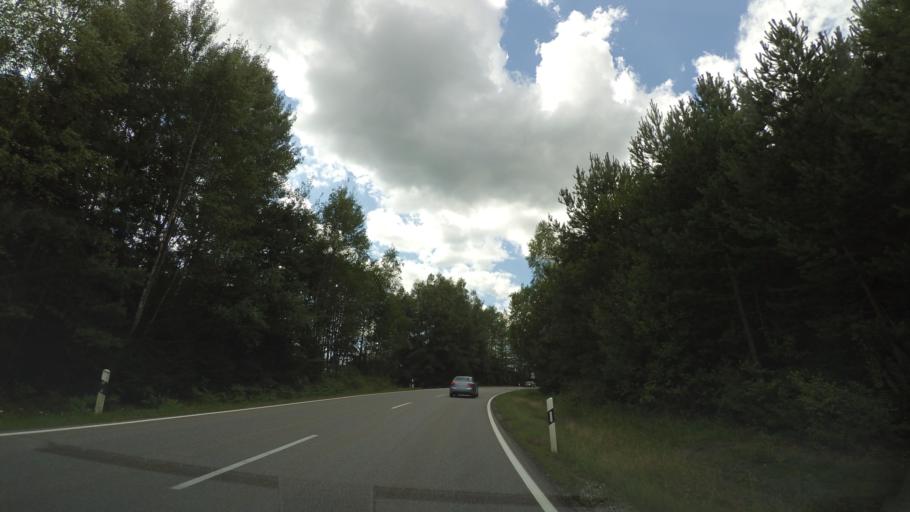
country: DE
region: Bavaria
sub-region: Lower Bavaria
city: Bobrach
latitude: 49.0555
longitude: 13.0465
